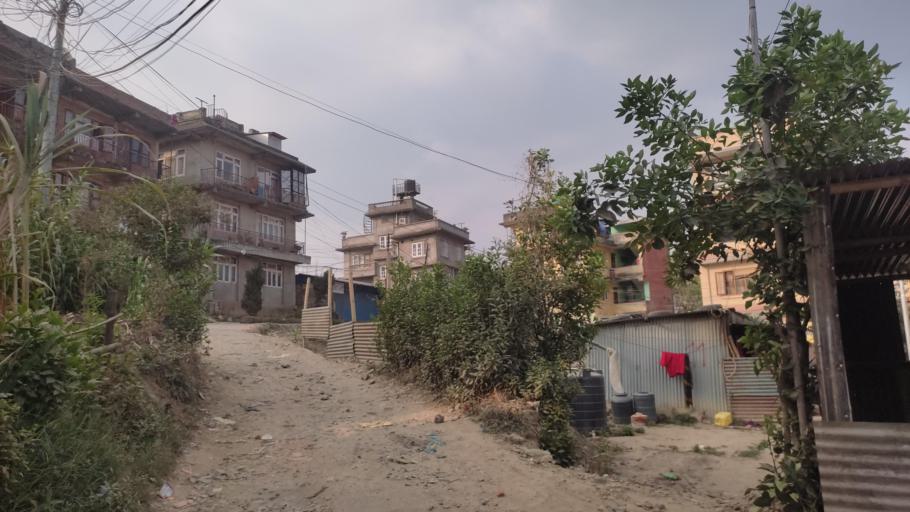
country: NP
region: Central Region
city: Kirtipur
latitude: 27.6725
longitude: 85.2771
